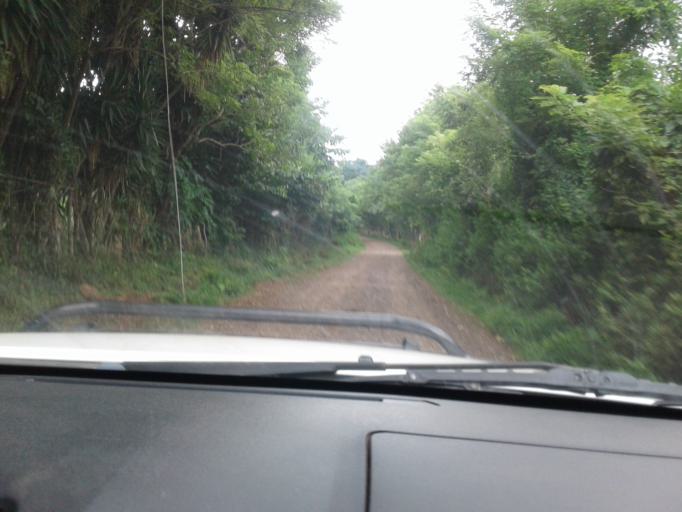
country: NI
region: Matagalpa
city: San Ramon
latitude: 12.9024
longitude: -85.7448
